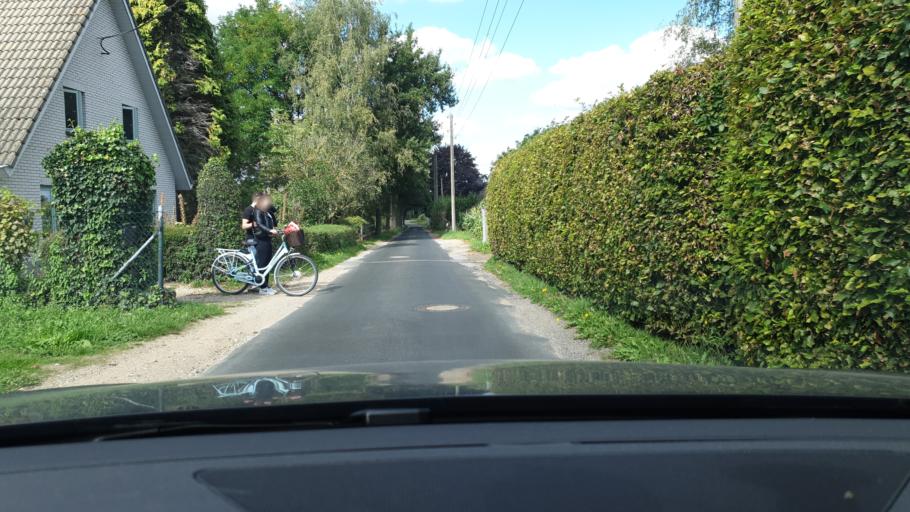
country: NL
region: Gelderland
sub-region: Gemeente Groesbeek
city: Bredeweg
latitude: 51.7499
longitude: 5.9567
